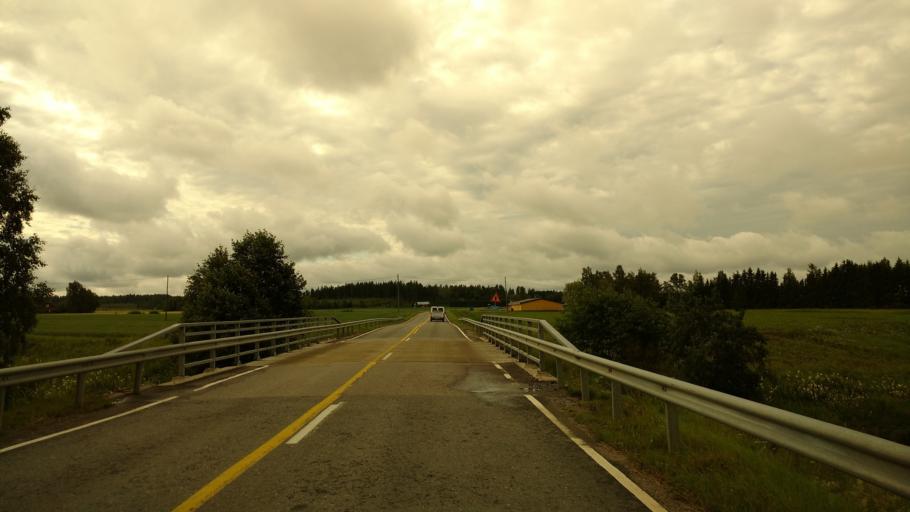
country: FI
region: Varsinais-Suomi
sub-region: Salo
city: Kuusjoki
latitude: 60.5139
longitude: 23.1796
